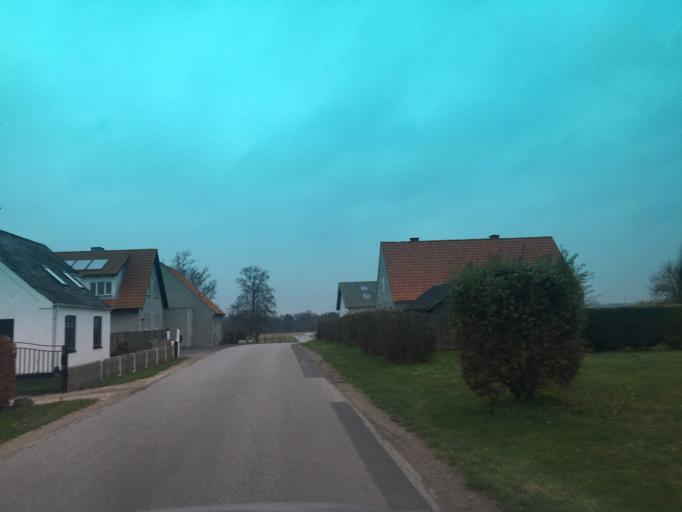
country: DK
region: Zealand
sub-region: Slagelse Kommune
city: Skaelskor
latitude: 55.2268
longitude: 11.4199
